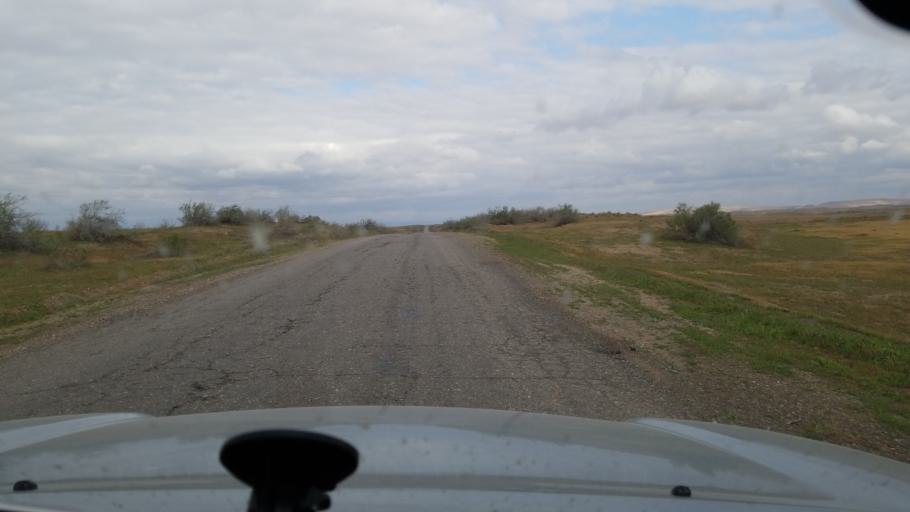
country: TM
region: Mary
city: Serhetabat
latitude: 35.9840
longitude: 62.6353
